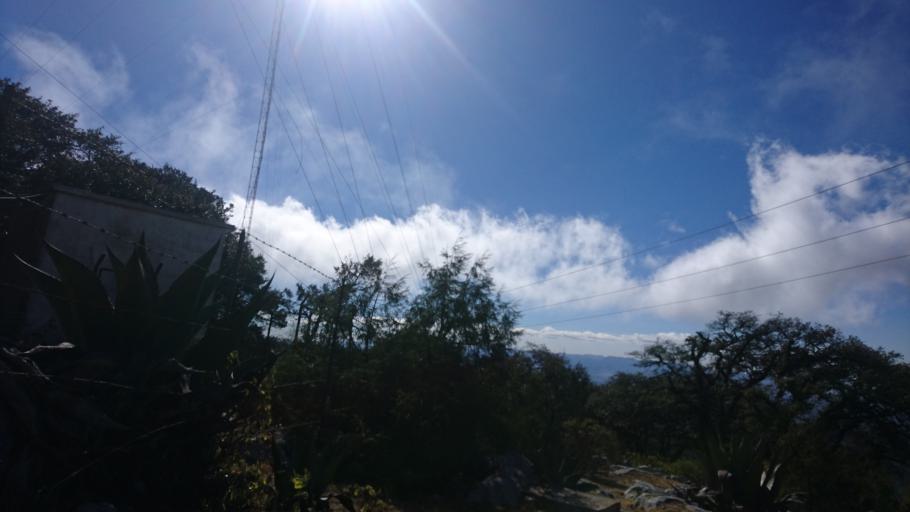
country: MX
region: San Luis Potosi
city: Zaragoza
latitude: 22.0660
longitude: -100.6502
